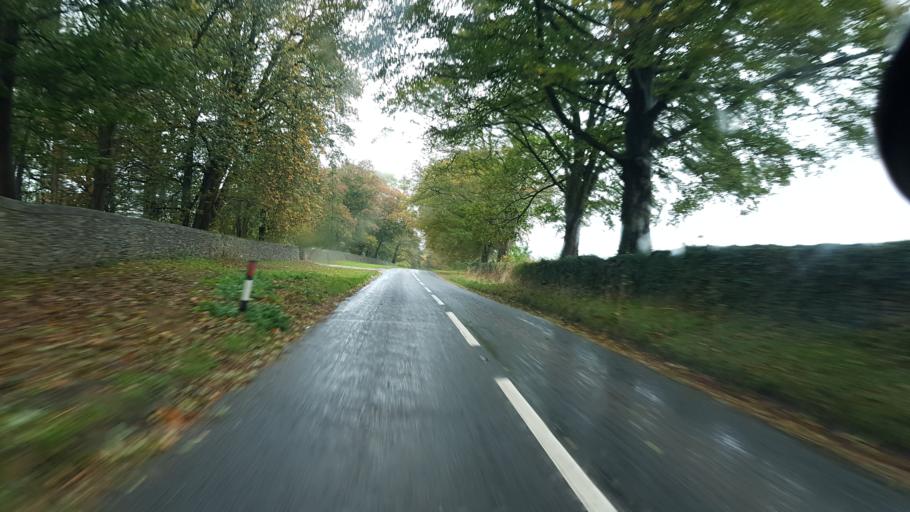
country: GB
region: England
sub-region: Gloucestershire
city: Stow on the Wold
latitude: 51.9345
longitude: -1.7295
